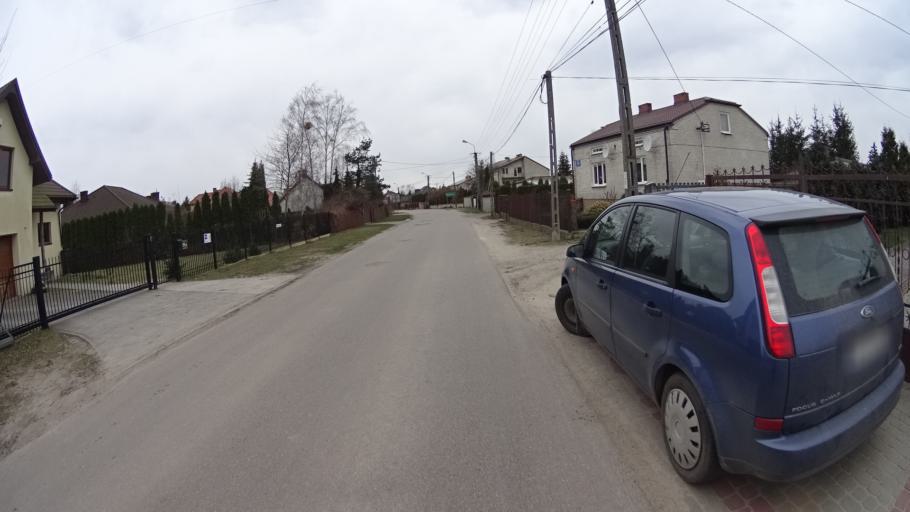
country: PL
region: Masovian Voivodeship
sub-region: Powiat warszawski zachodni
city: Truskaw
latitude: 52.2605
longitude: 20.7477
